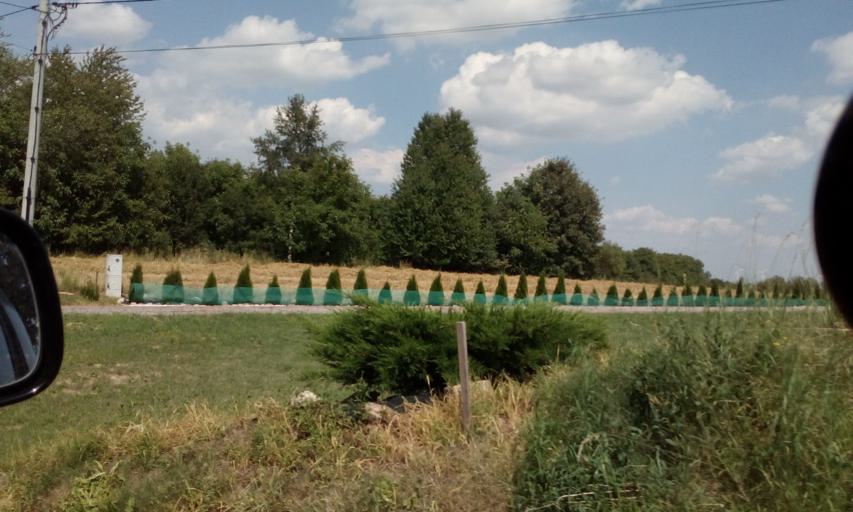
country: PL
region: Subcarpathian Voivodeship
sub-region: Powiat lancucki
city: Wysoka
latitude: 50.0484
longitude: 22.2405
